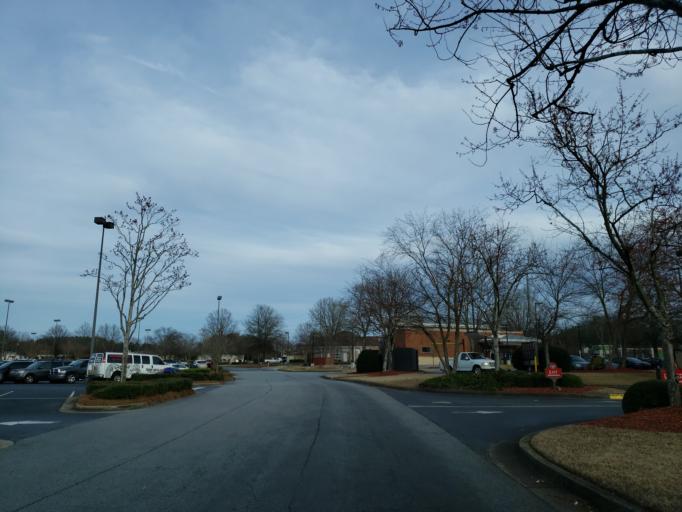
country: US
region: Georgia
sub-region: Cherokee County
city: Woodstock
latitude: 34.0371
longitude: -84.4646
